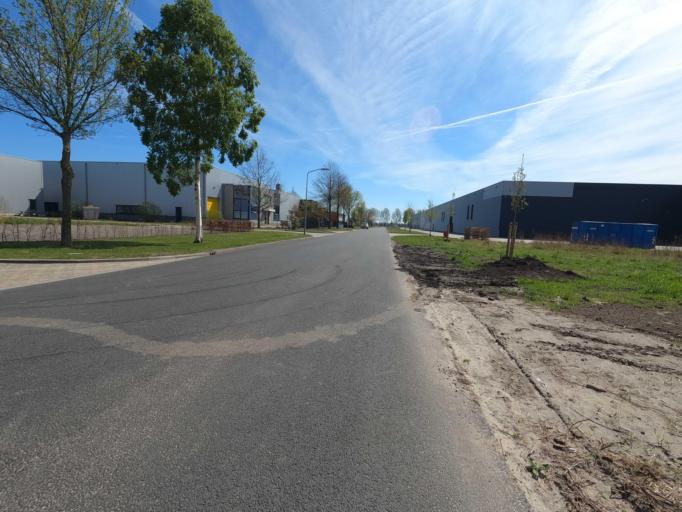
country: NL
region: Flevoland
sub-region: Gemeente Zeewolde
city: Zeewolde
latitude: 52.3513
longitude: 5.4998
